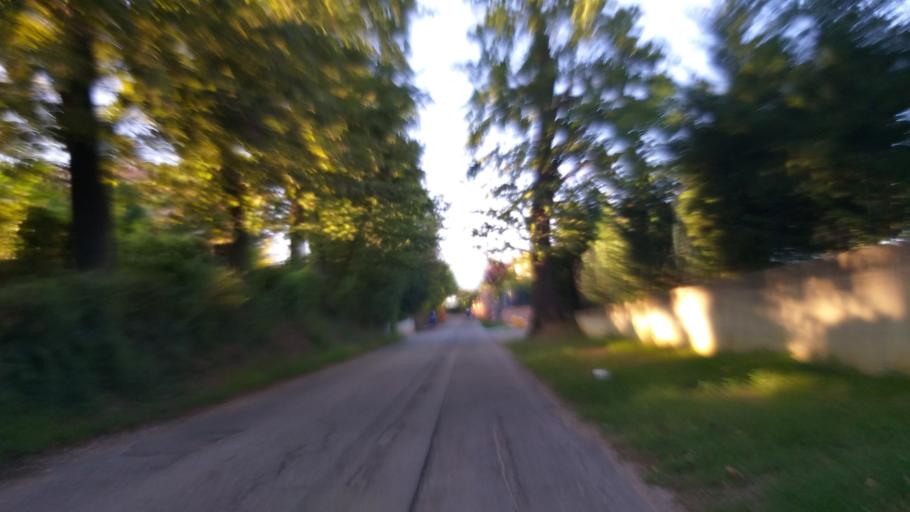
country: IT
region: Piedmont
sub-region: Provincia di Asti
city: Asti
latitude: 44.9207
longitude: 8.1998
